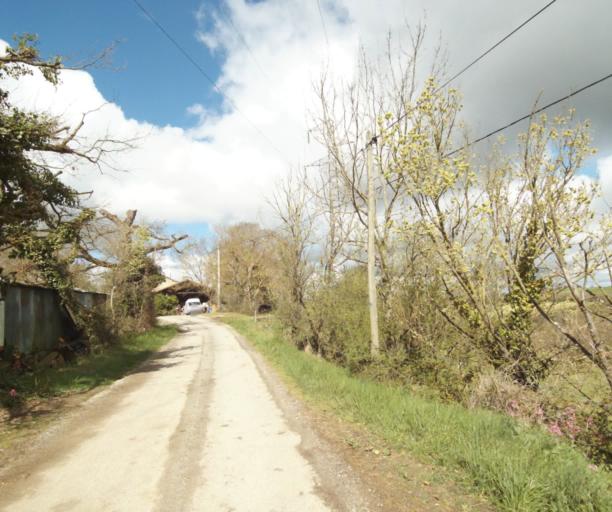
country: FR
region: Midi-Pyrenees
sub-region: Departement de l'Ariege
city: Saverdun
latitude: 43.1826
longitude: 1.5451
